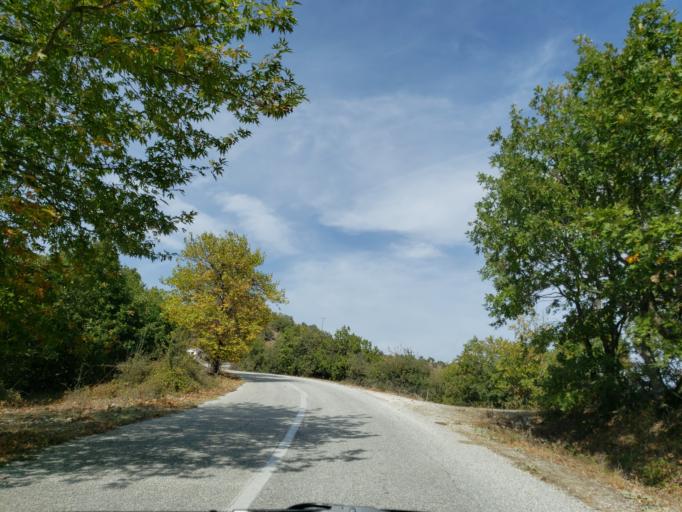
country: GR
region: Thessaly
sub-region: Trikala
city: Kastraki
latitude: 39.7417
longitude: 21.6573
